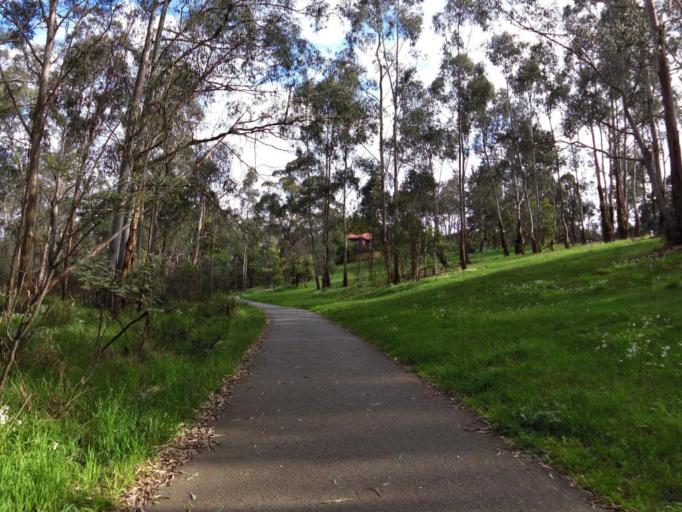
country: AU
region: Victoria
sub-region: Manningham
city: Donvale
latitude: -37.7595
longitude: 145.1822
